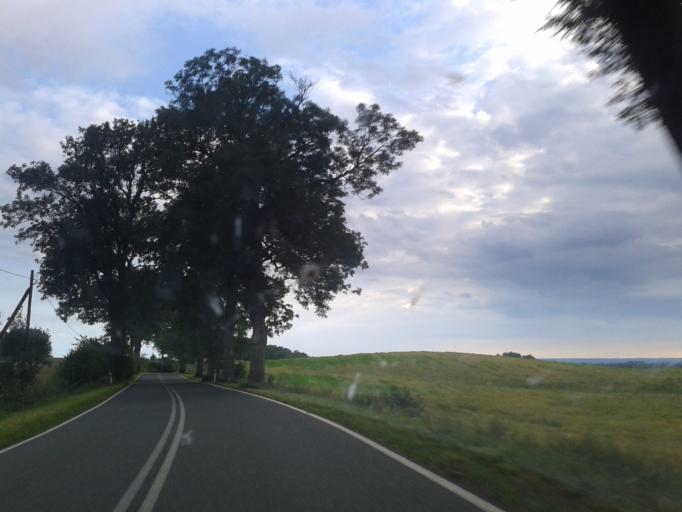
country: PL
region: West Pomeranian Voivodeship
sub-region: Powiat szczecinecki
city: Grzmiaca
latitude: 53.8820
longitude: 16.4998
